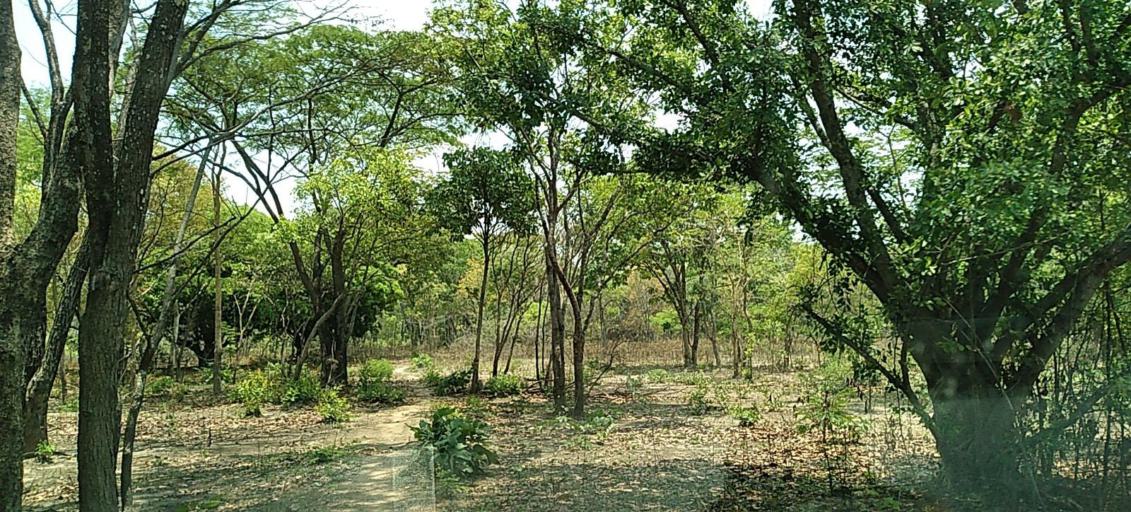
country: ZM
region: Copperbelt
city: Luanshya
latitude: -13.1597
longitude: 28.1844
